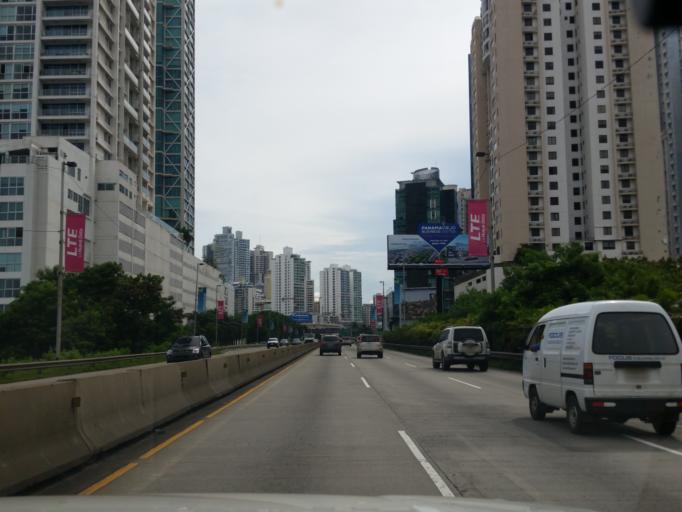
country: PA
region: Panama
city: Panama
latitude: 8.9818
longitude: -79.5062
